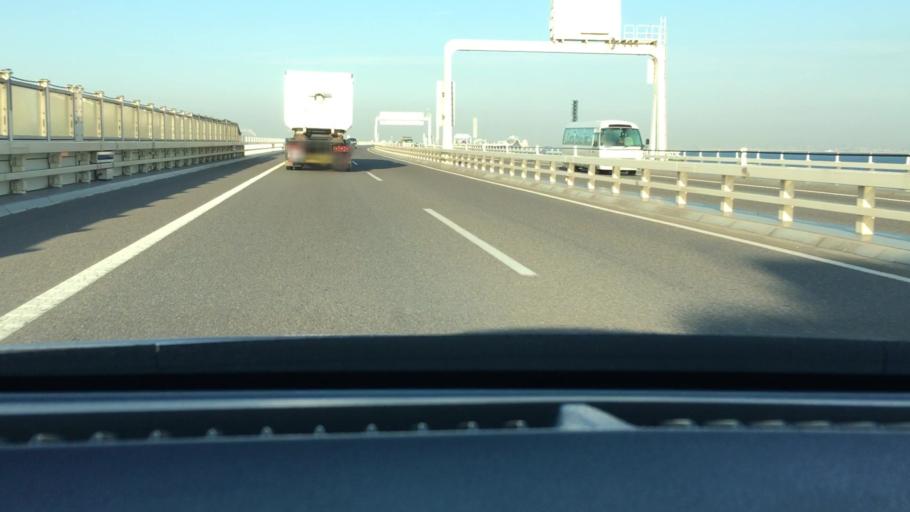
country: JP
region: Chiba
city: Kisarazu
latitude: 35.4372
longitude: 139.9151
